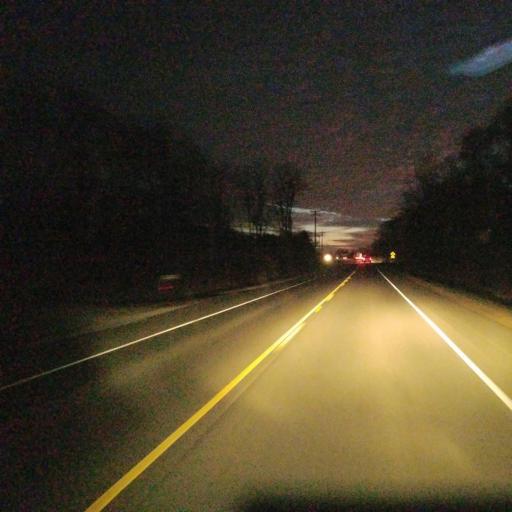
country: US
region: Illinois
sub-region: Peoria County
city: Elmwood
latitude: 40.6979
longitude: -89.9042
